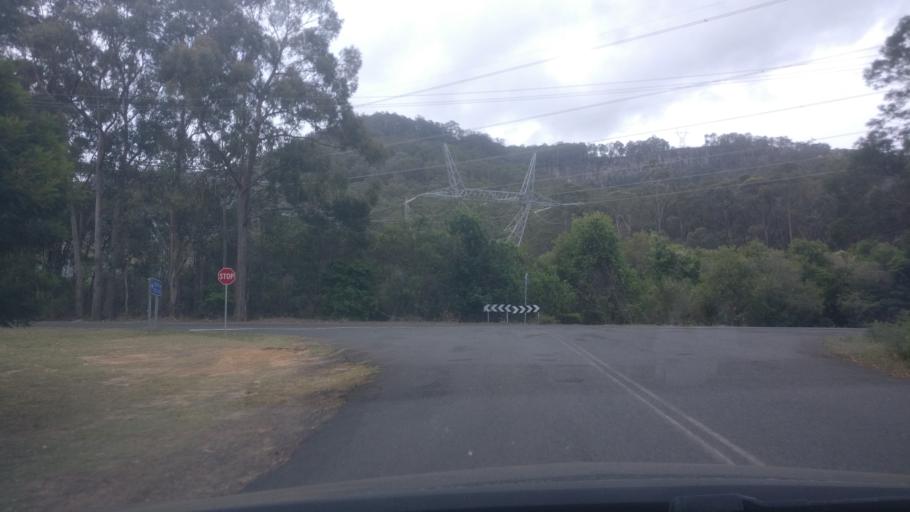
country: AU
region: New South Wales
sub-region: Shoalhaven Shire
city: Kangaroo Valley
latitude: -34.7256
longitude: 150.4823
